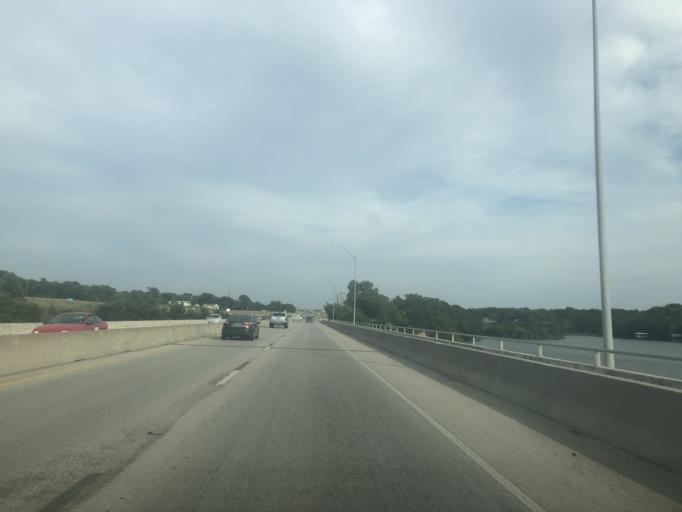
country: US
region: Texas
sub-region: Tarrant County
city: Lake Worth
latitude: 32.8209
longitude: -97.4464
